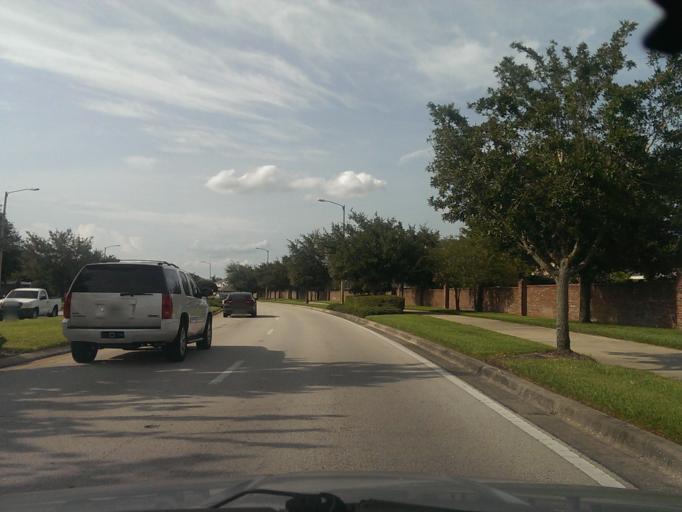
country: US
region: Florida
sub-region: Orange County
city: Winter Garden
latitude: 28.5316
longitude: -81.5818
